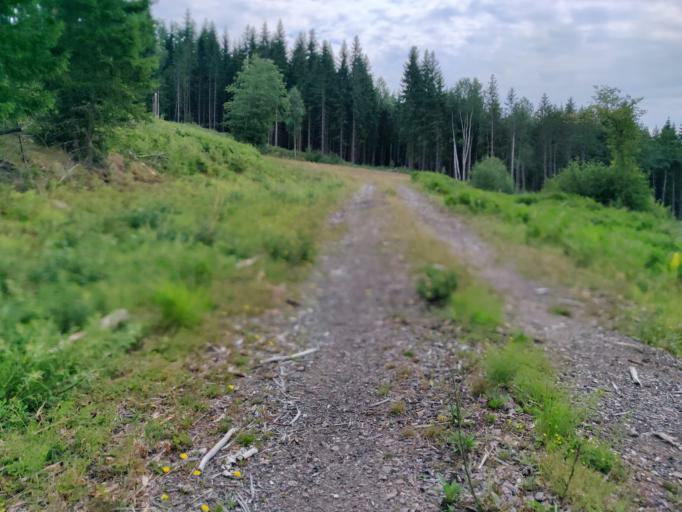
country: SE
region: Vaermland
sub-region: Hagfors Kommun
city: Hagfors
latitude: 59.9613
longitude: 13.5737
